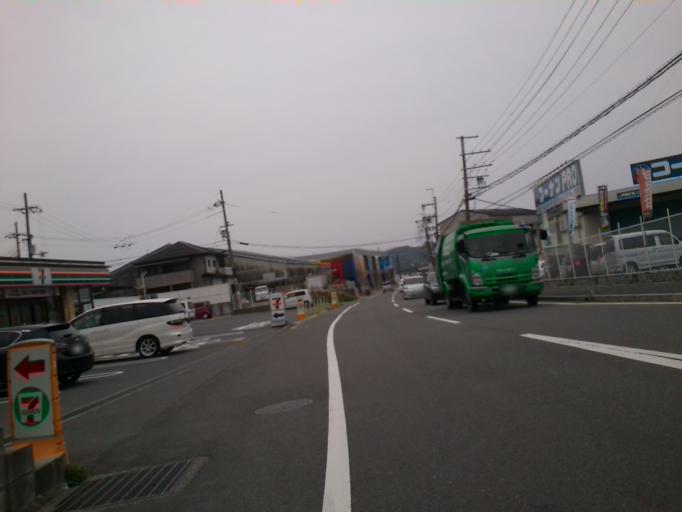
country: JP
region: Kyoto
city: Yawata
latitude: 34.8555
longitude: 135.7143
